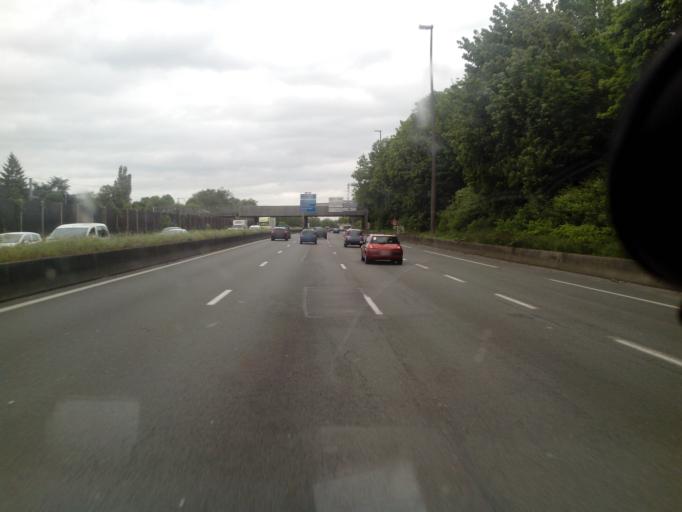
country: FR
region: Nord-Pas-de-Calais
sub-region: Departement du Nord
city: La Madeleine
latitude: 50.6456
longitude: 3.0960
